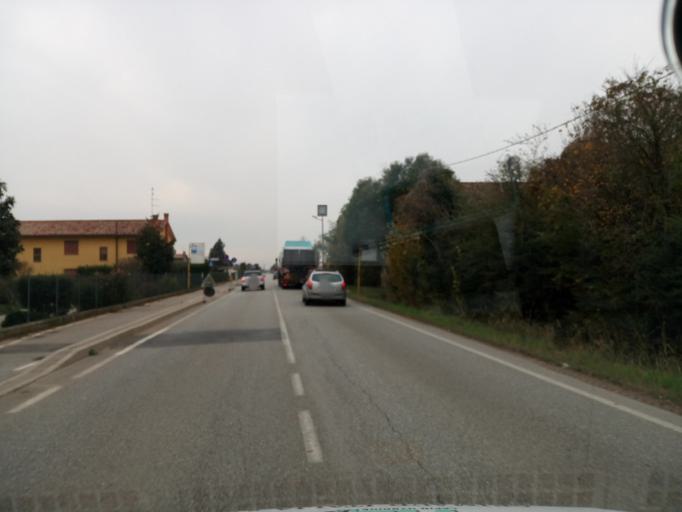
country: IT
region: Veneto
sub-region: Provincia di Treviso
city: Fanzolo
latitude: 45.7173
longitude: 12.0148
